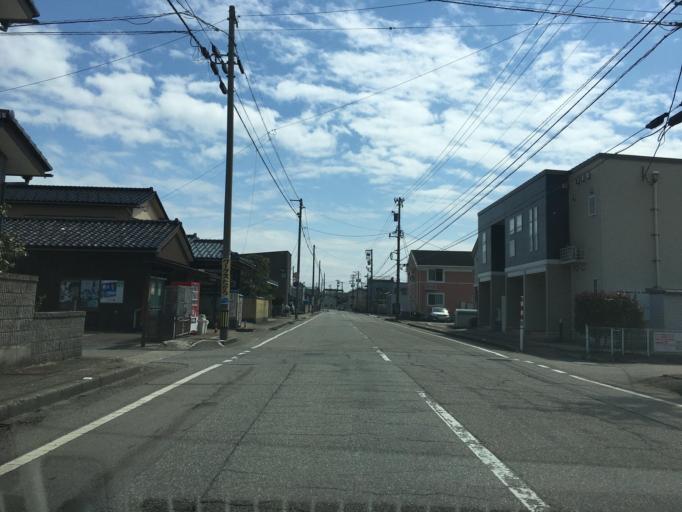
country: JP
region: Toyama
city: Nishishinminato
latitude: 36.7992
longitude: 137.0555
